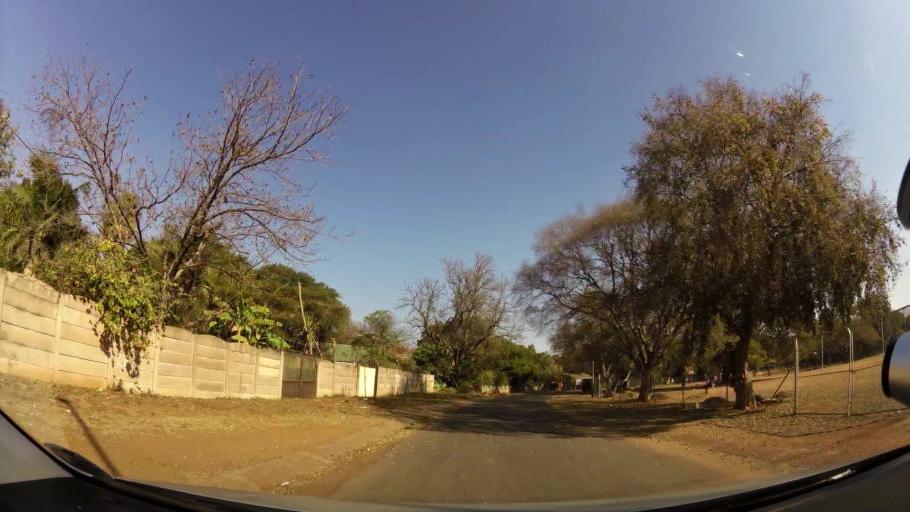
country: ZA
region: Gauteng
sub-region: City of Tshwane Metropolitan Municipality
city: Pretoria
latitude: -25.6666
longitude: 28.1741
